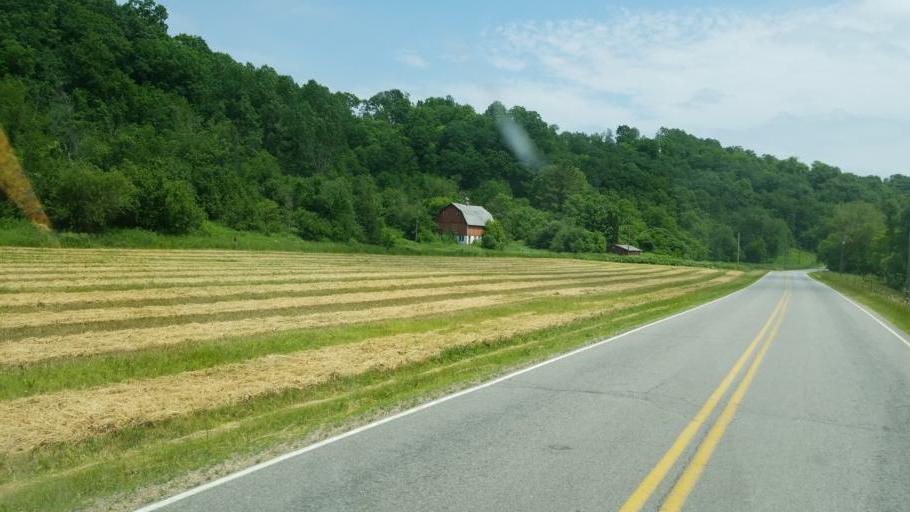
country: US
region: Wisconsin
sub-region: Monroe County
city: Cashton
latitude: 43.6603
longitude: -90.7182
